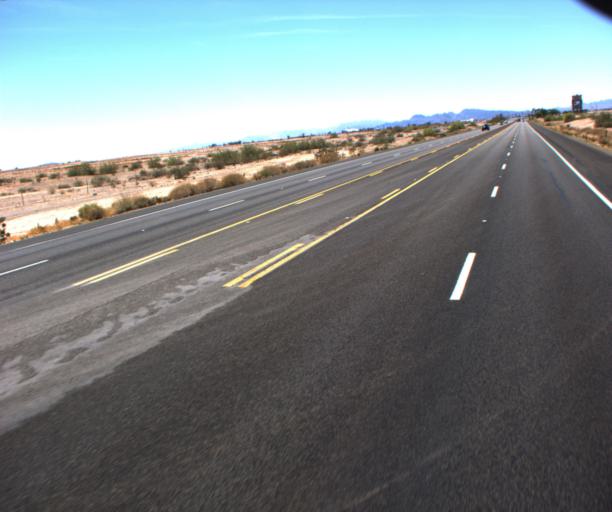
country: US
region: Arizona
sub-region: La Paz County
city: Parker
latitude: 34.1630
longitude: -114.2591
